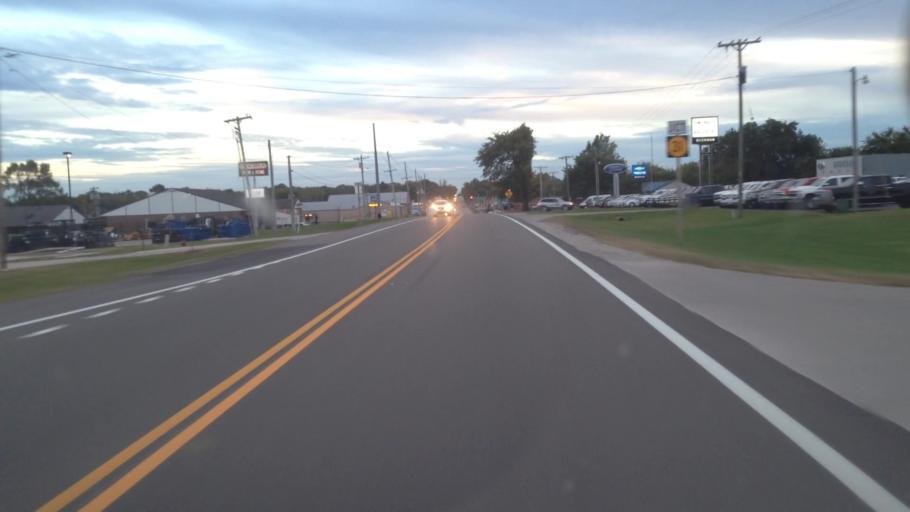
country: US
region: Kansas
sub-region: Anderson County
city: Garnett
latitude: 38.2914
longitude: -95.2493
